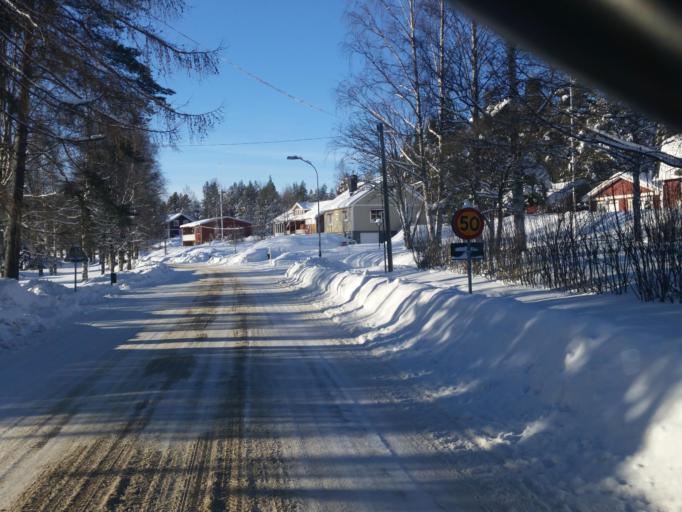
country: SE
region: Norrbotten
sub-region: Pitea Kommun
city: Bergsviken
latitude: 65.3075
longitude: 21.3807
